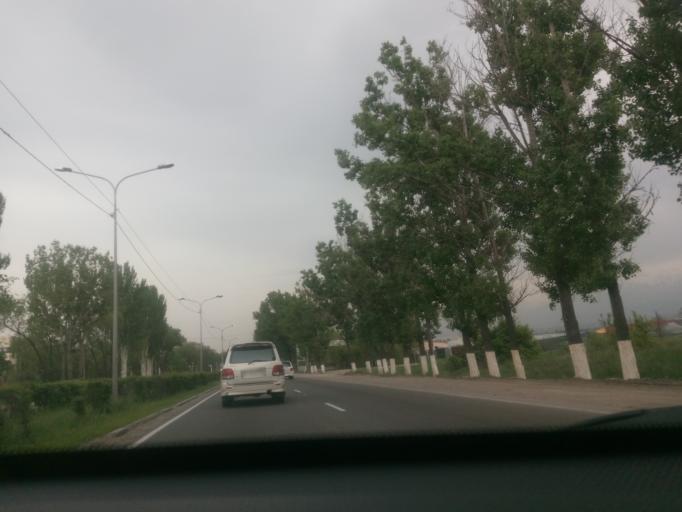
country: KZ
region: Almaty Oblysy
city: Burunday
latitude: 43.2272
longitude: 76.7476
